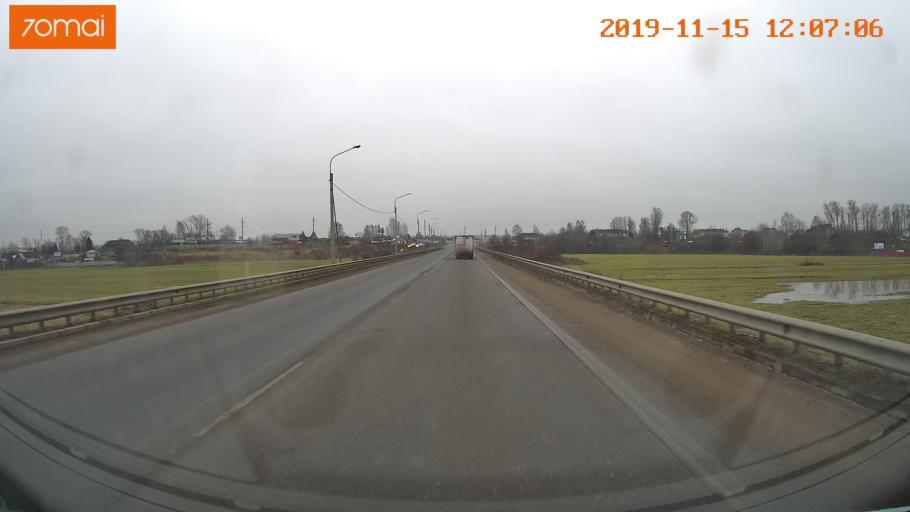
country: RU
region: Vologda
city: Molochnoye
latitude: 59.2366
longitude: 39.7715
